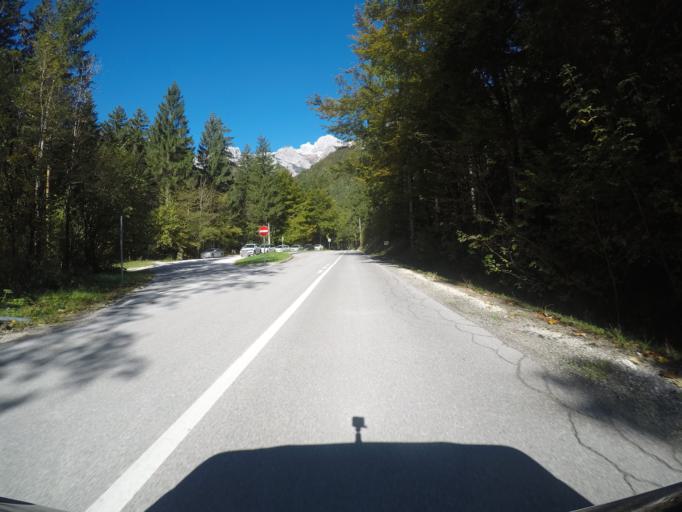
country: SI
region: Kamnik
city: Mekinje
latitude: 46.3258
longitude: 14.5915
